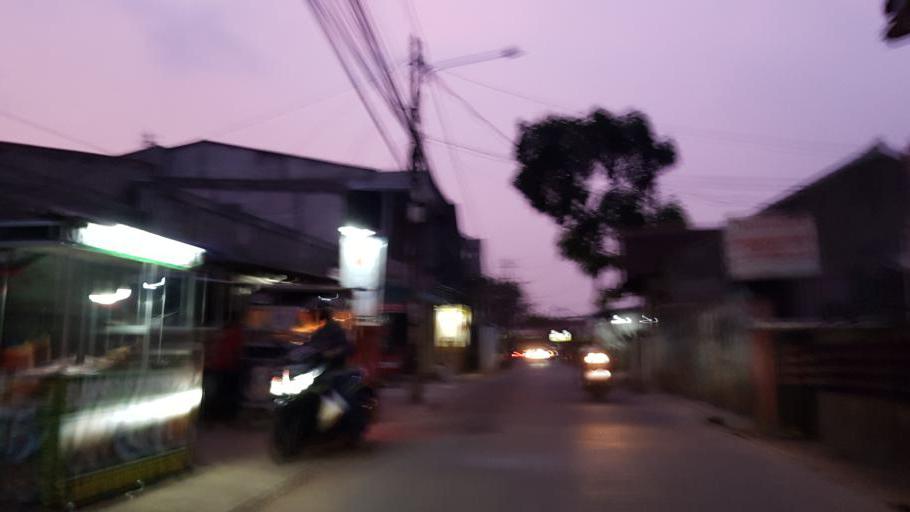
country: ID
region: West Java
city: Pamulang
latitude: -6.3423
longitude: 106.7869
